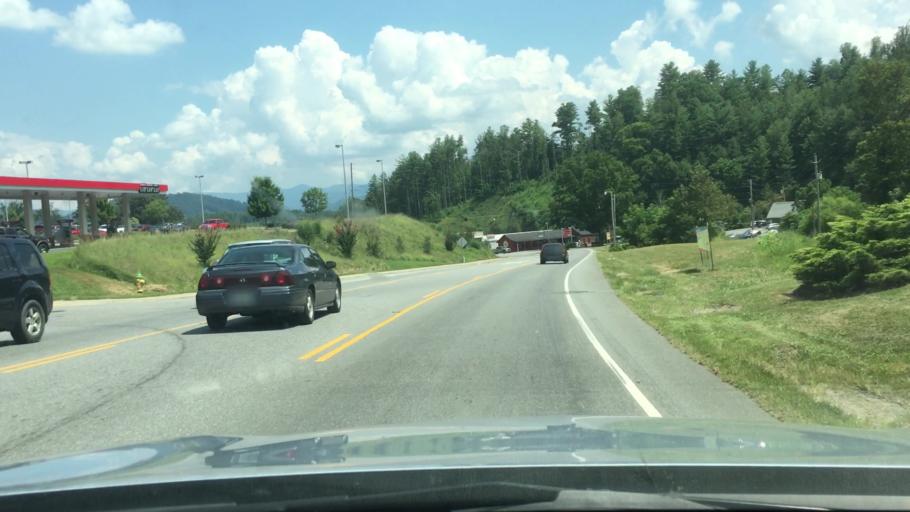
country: US
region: North Carolina
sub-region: Madison County
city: Mars Hill
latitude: 35.8246
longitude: -82.5455
